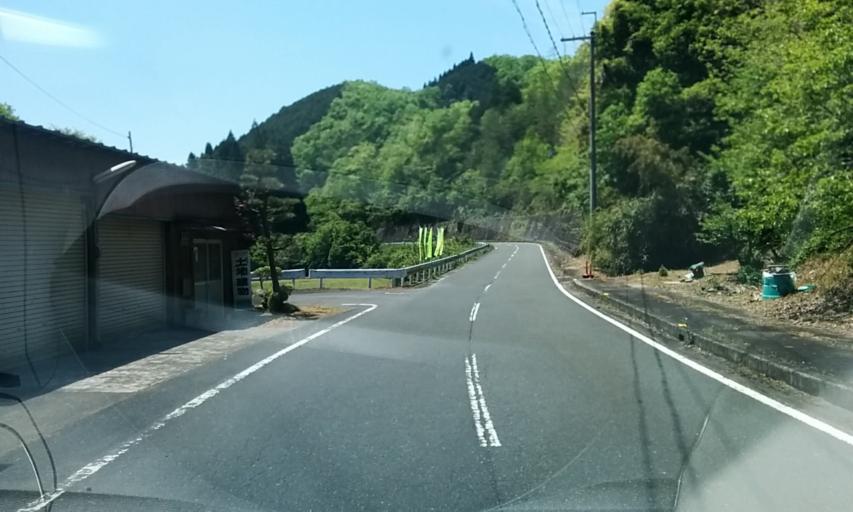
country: JP
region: Kyoto
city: Ayabe
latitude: 35.2170
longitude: 135.2962
